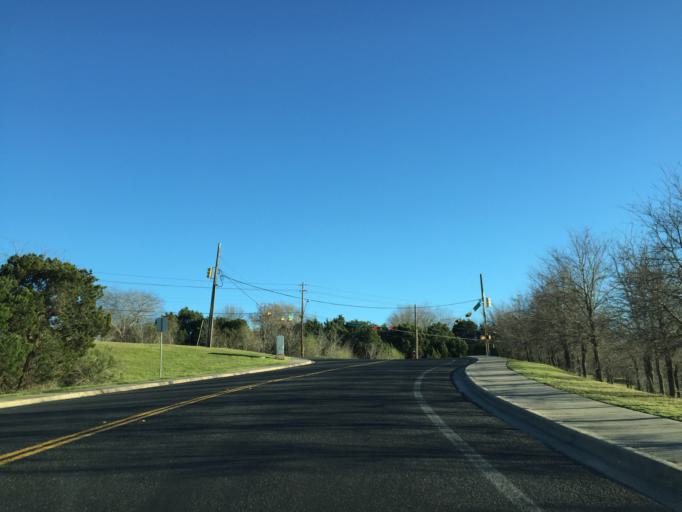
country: US
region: Texas
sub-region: Williamson County
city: Jollyville
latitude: 30.4308
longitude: -97.7815
